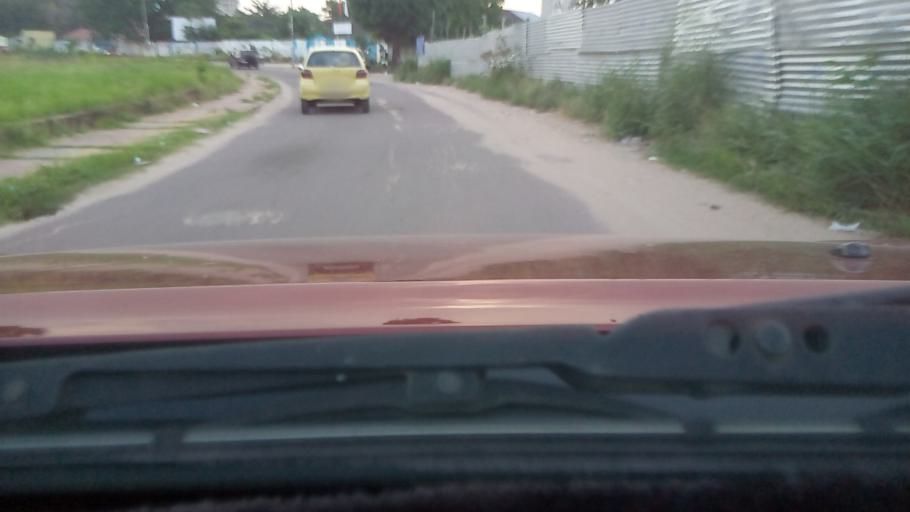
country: CD
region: Kinshasa
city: Kinshasa
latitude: -4.3100
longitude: 15.2807
